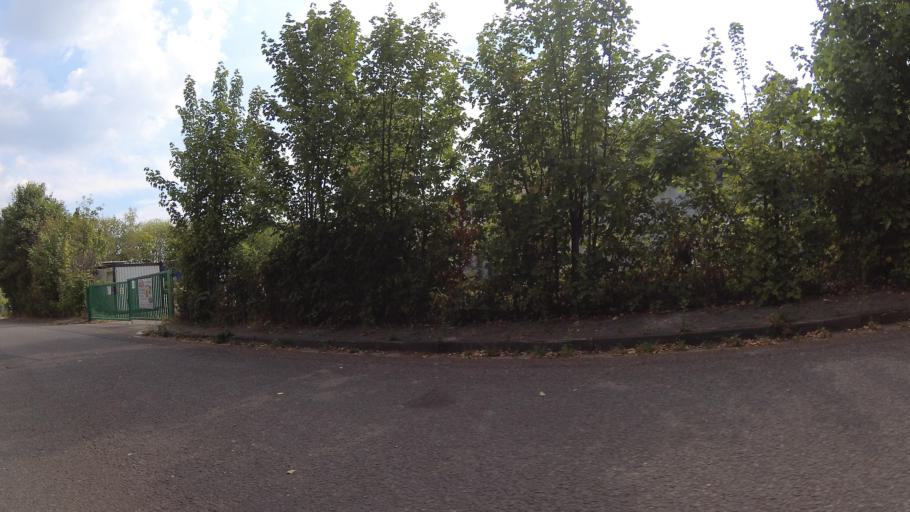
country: DE
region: Rheinland-Pfalz
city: Waldmohr
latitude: 49.3827
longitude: 7.3457
